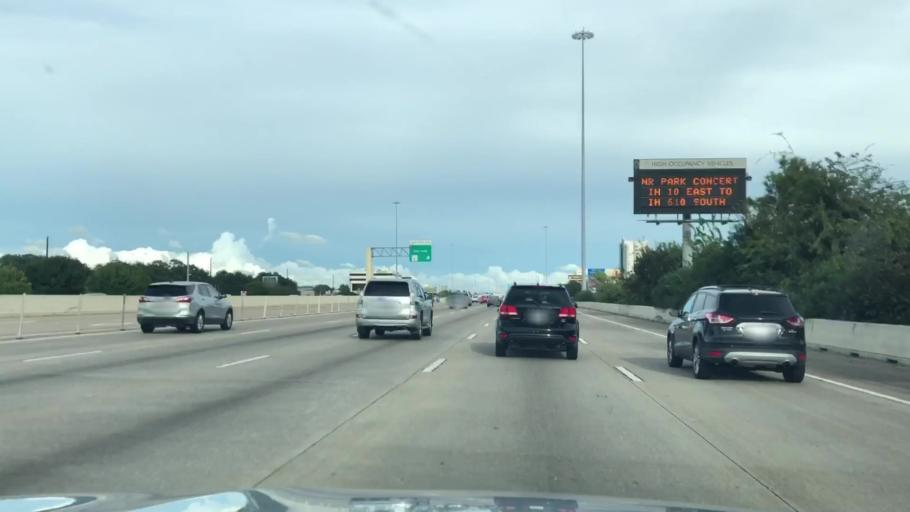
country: US
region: Texas
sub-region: Fort Bend County
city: Mission Bend
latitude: 29.7857
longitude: -95.6758
